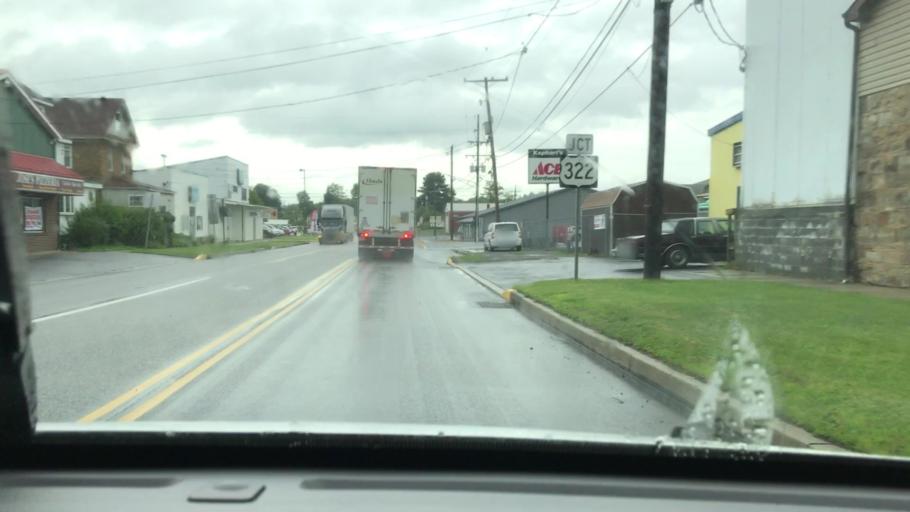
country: US
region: Pennsylvania
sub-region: Centre County
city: Philipsburg
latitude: 40.8998
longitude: -78.2232
